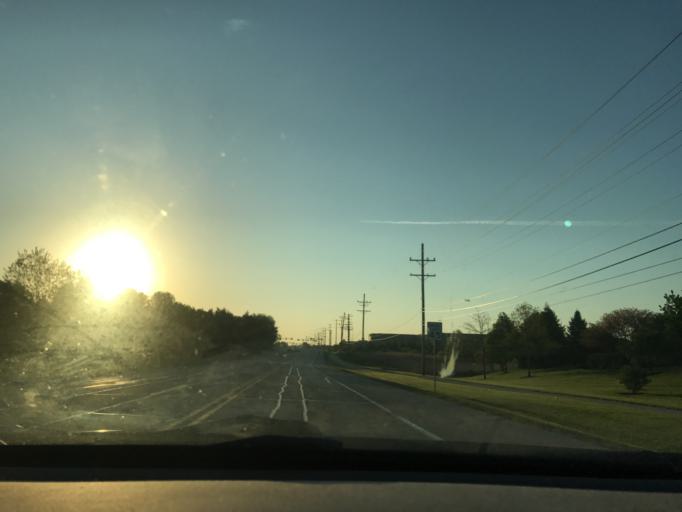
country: US
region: Illinois
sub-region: Kane County
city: South Elgin
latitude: 42.0070
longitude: -88.3440
